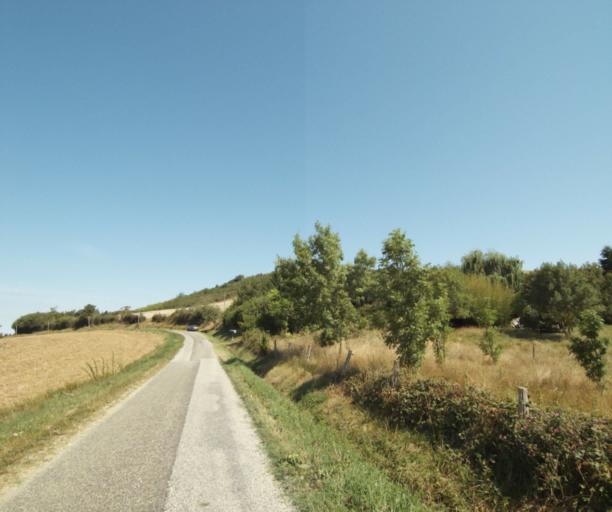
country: FR
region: Midi-Pyrenees
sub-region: Departement de l'Ariege
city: Lezat-sur-Leze
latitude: 43.2528
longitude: 1.3724
